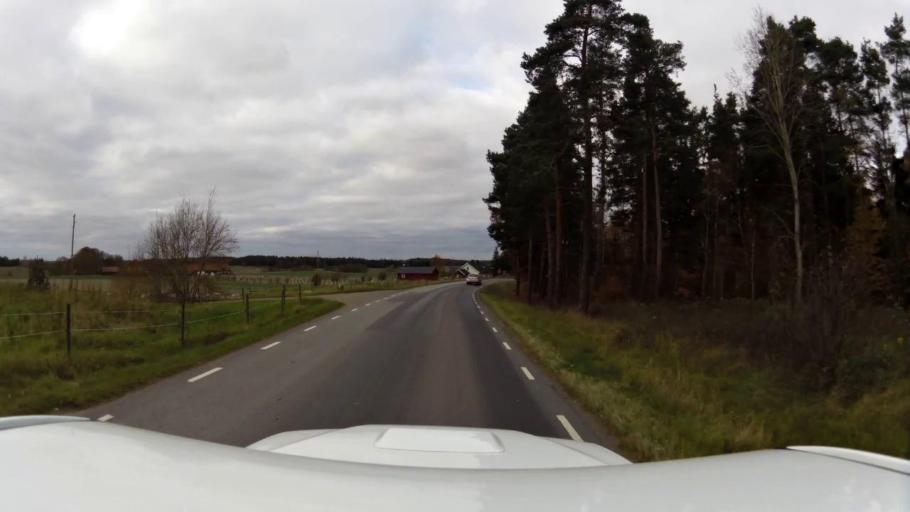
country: SE
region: OEstergoetland
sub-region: Linkopings Kommun
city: Linghem
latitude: 58.4160
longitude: 15.7401
